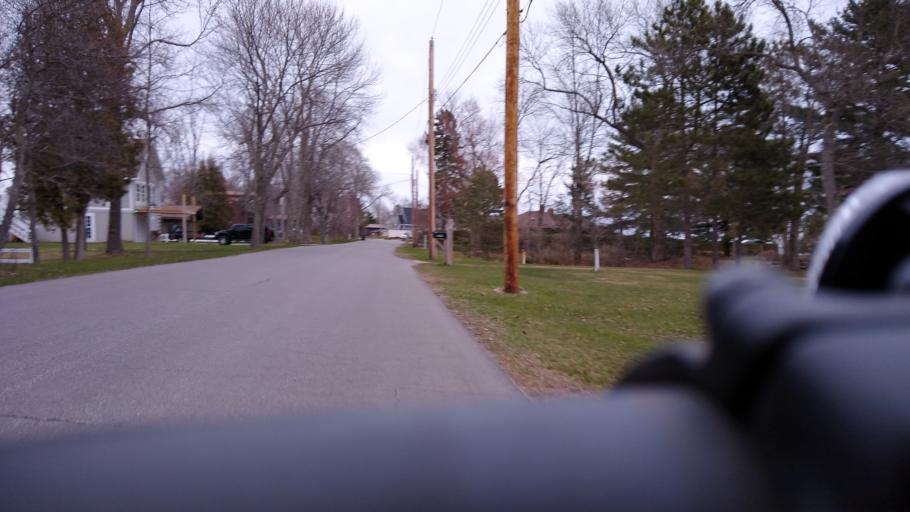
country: US
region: Michigan
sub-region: Delta County
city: Escanaba
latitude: 45.7023
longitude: -87.0941
